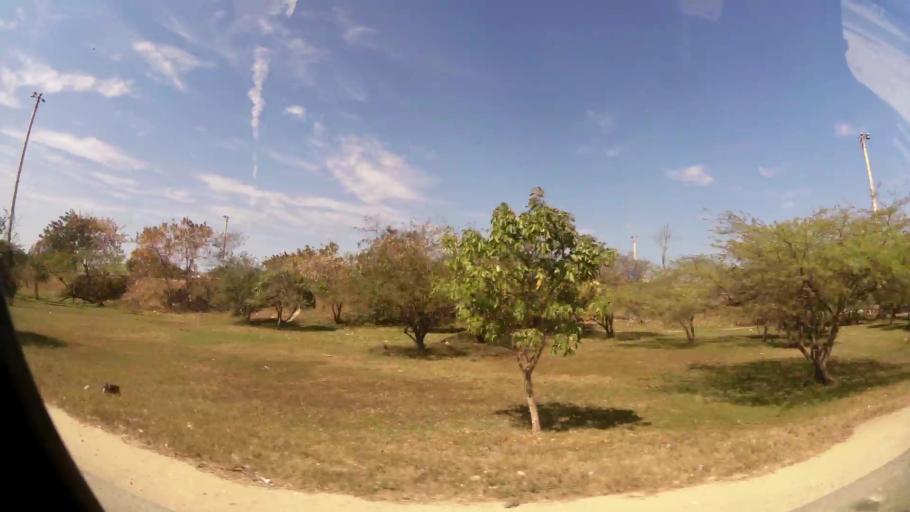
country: CO
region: Atlantico
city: Barranquilla
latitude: 10.9428
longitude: -74.8346
